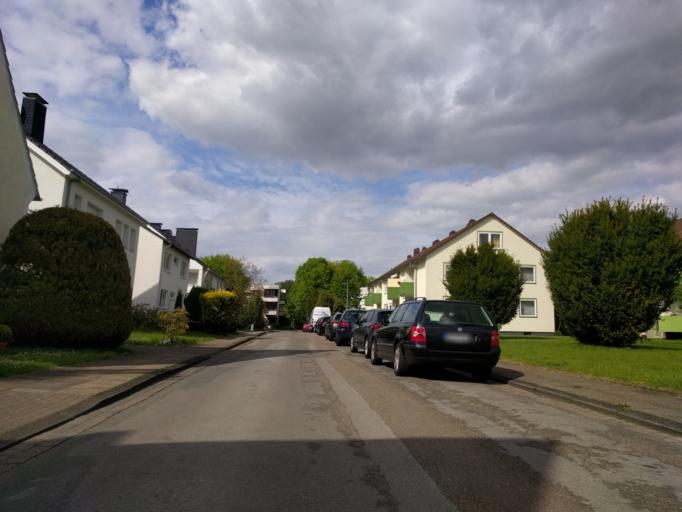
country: DE
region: North Rhine-Westphalia
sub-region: Regierungsbezirk Detmold
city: Bielefeld
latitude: 52.0562
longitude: 8.5213
